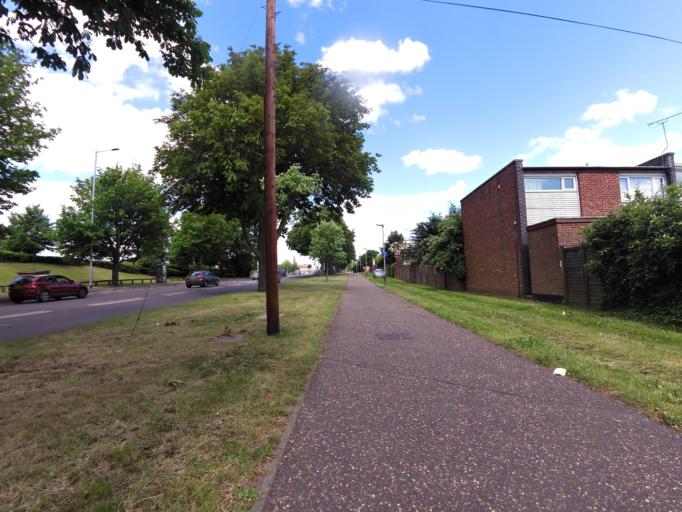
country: GB
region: England
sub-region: Norfolk
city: Norwich
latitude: 52.6543
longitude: 1.2700
